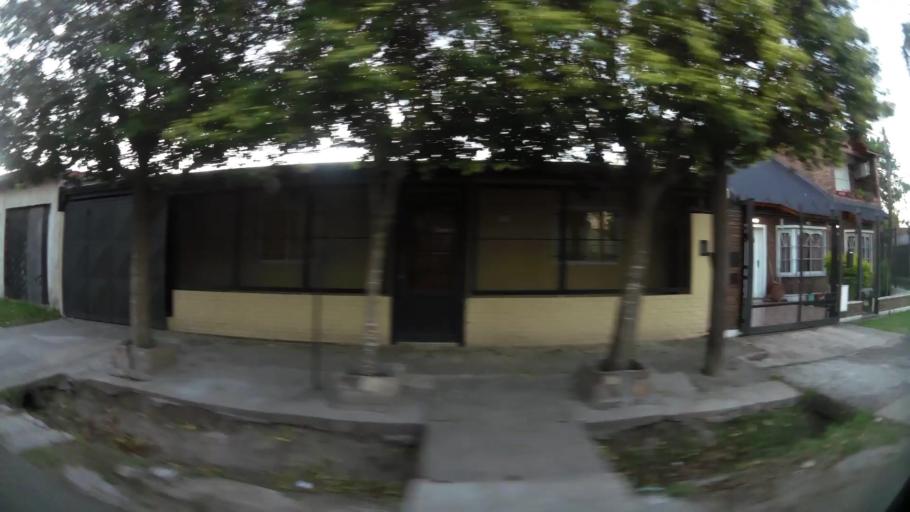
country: AR
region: Santa Fe
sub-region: Departamento de Rosario
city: Rosario
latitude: -32.9684
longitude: -60.6873
